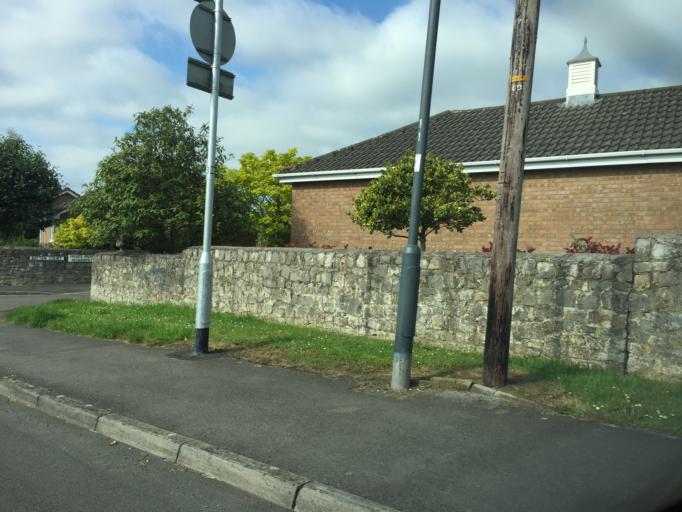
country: GB
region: England
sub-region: South Gloucestershire
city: Chipping Sodbury
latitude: 51.5391
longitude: -2.3886
